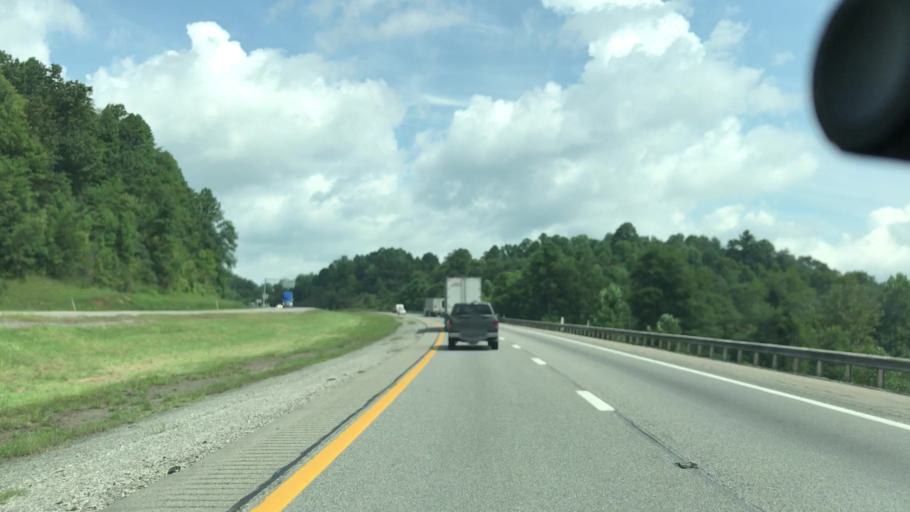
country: US
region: West Virginia
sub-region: Raleigh County
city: Bradley
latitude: 37.9440
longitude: -81.2559
